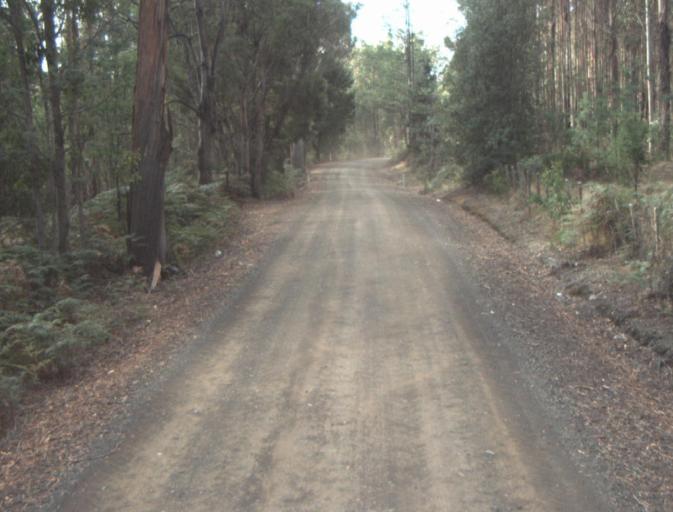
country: AU
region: Tasmania
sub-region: Launceston
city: Mayfield
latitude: -41.2149
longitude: 147.1773
